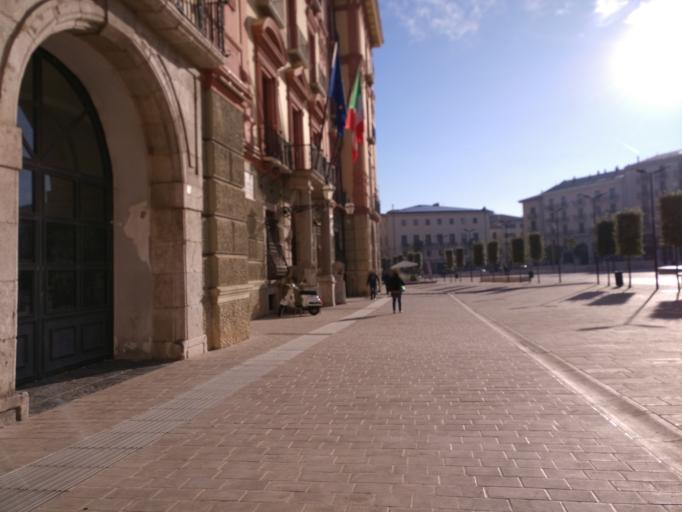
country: IT
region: Campania
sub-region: Provincia di Avellino
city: Avellino
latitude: 40.9148
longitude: 14.7920
